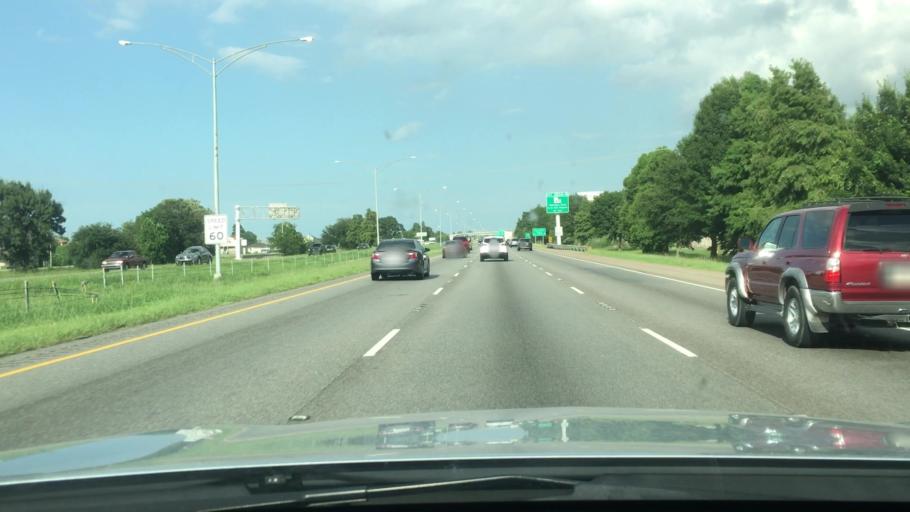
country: US
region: Louisiana
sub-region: Jefferson Parish
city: Kenner
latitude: 30.0085
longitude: -90.2545
